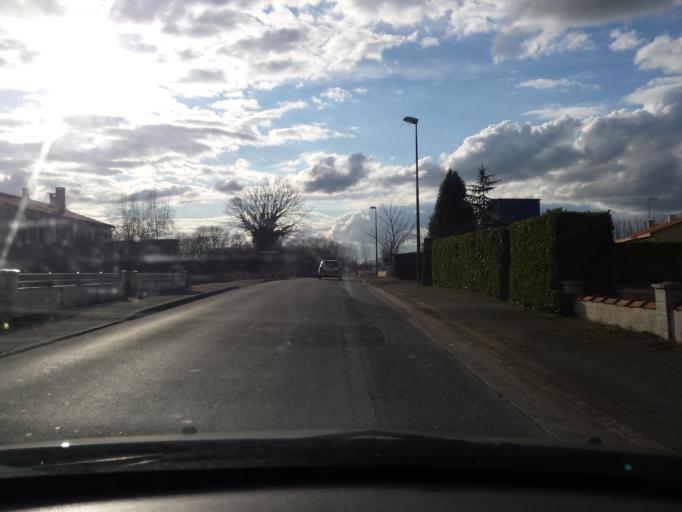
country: FR
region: Pays de la Loire
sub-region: Departement de la Vendee
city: Saint-Martin-des-Noyers
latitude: 46.7218
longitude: -1.1860
